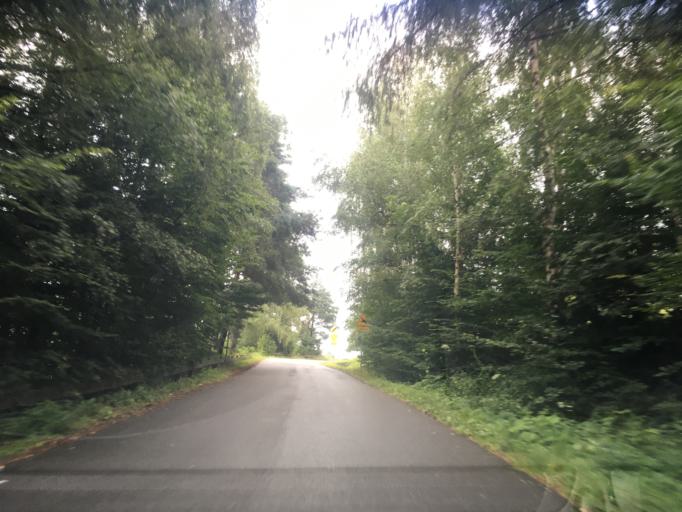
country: PL
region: Lesser Poland Voivodeship
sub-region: Powiat myslenicki
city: Brzaczowice
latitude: 49.8487
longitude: 20.0421
